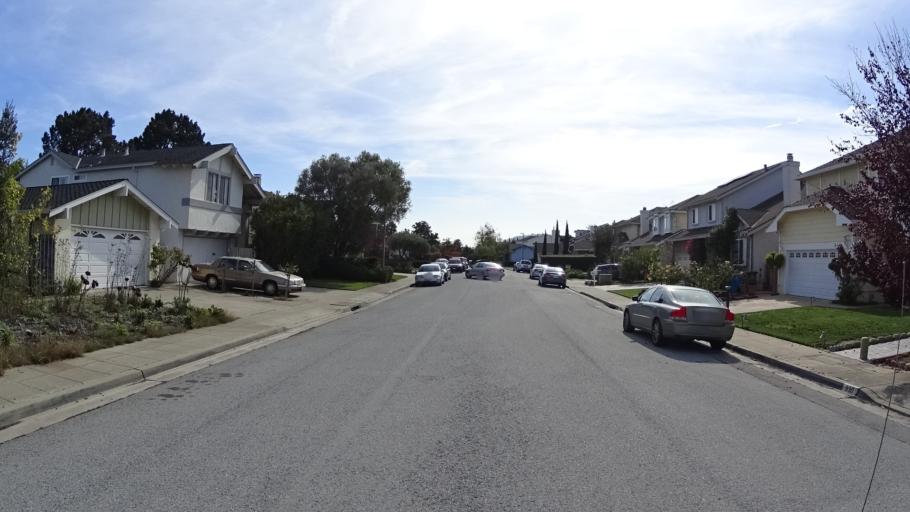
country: US
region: California
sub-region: San Mateo County
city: Foster City
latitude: 37.5437
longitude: -122.2765
